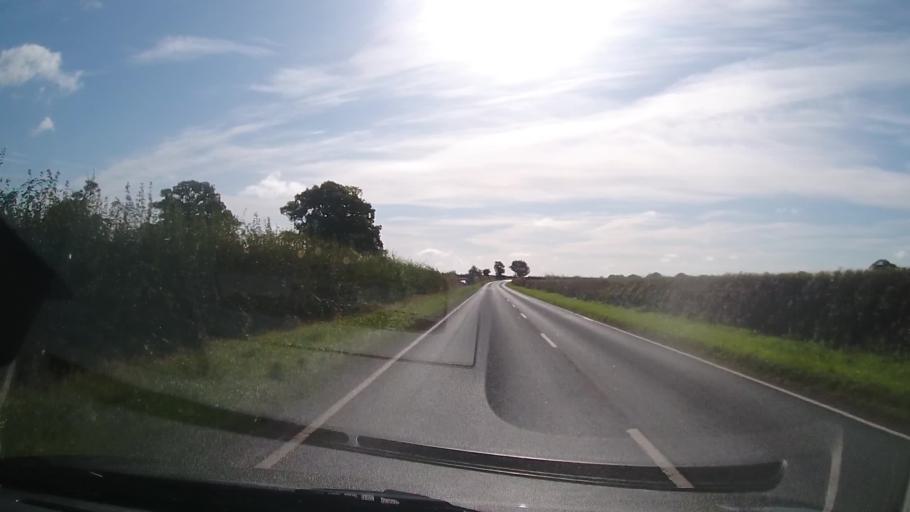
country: GB
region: England
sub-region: Shropshire
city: Wem
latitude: 52.8363
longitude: -2.7026
